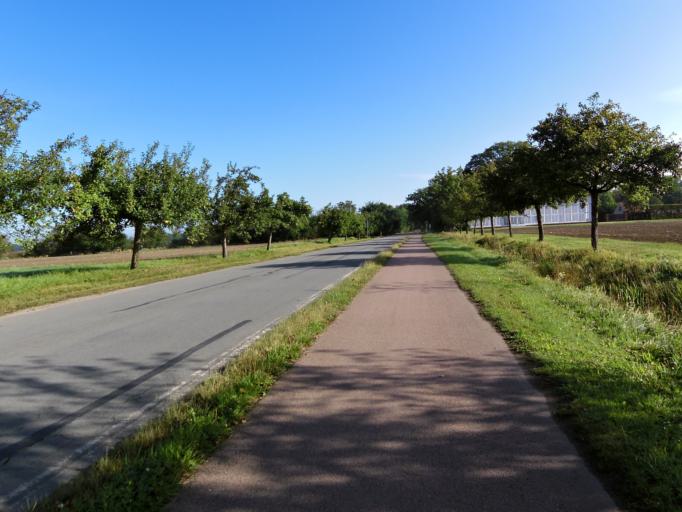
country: DE
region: Saxony-Anhalt
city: Worlitz
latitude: 51.8500
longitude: 12.4165
